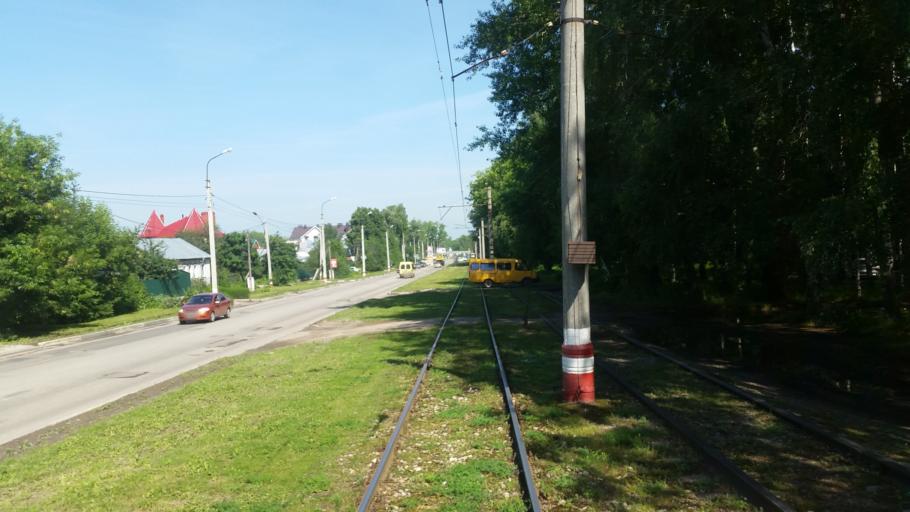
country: RU
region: Ulyanovsk
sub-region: Ulyanovskiy Rayon
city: Ulyanovsk
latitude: 54.3539
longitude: 48.3788
